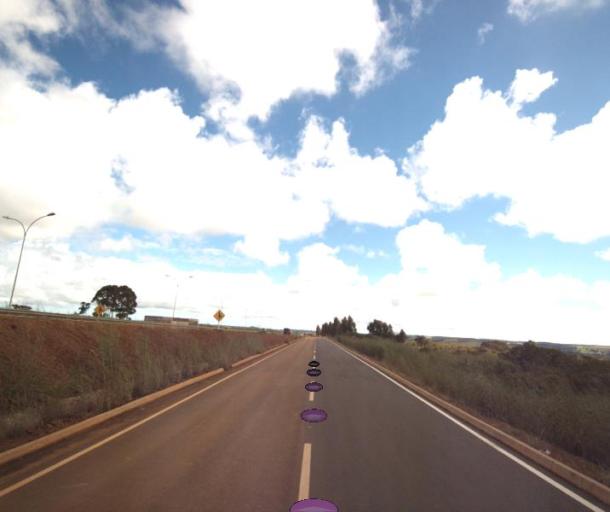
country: BR
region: Goias
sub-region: Anapolis
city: Anapolis
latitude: -16.2323
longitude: -49.0076
